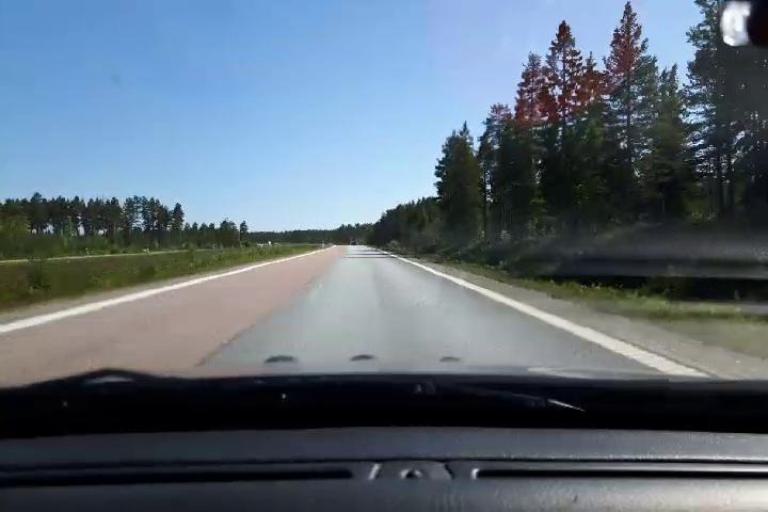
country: SE
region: Gaevleborg
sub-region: Soderhamns Kommun
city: Soderhamn
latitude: 61.3842
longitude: 16.9920
